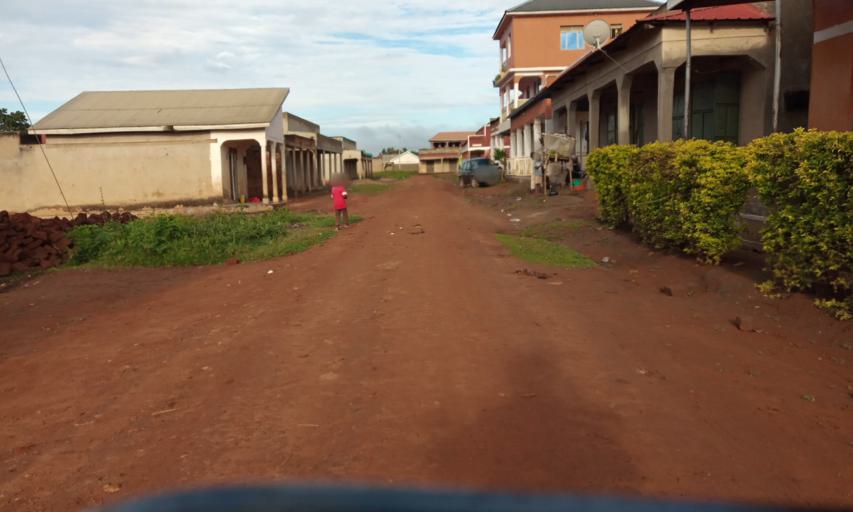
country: UG
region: Eastern Region
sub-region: Mbale District
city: Mbale
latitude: 1.1402
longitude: 34.1681
